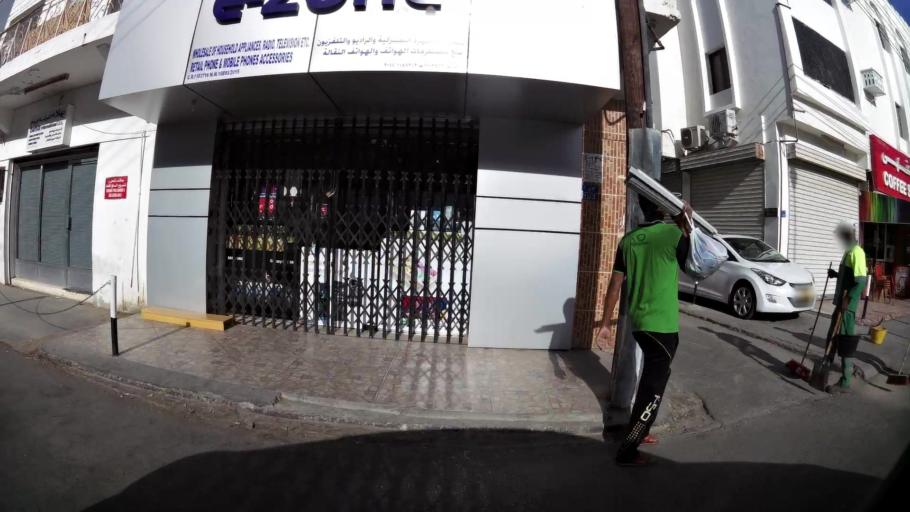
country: OM
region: Muhafazat Masqat
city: Muscat
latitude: 23.5906
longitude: 58.5430
